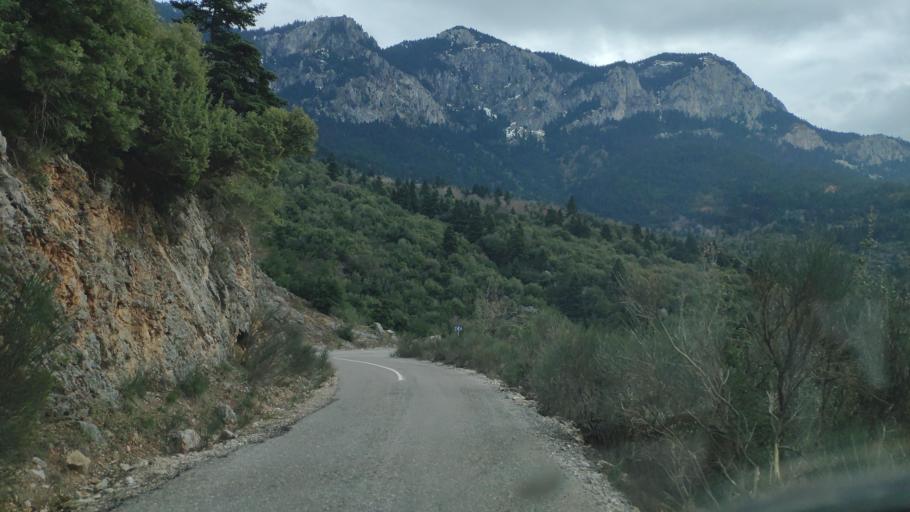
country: GR
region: Central Greece
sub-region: Nomos Fokidos
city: Amfissa
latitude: 38.6402
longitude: 22.4193
